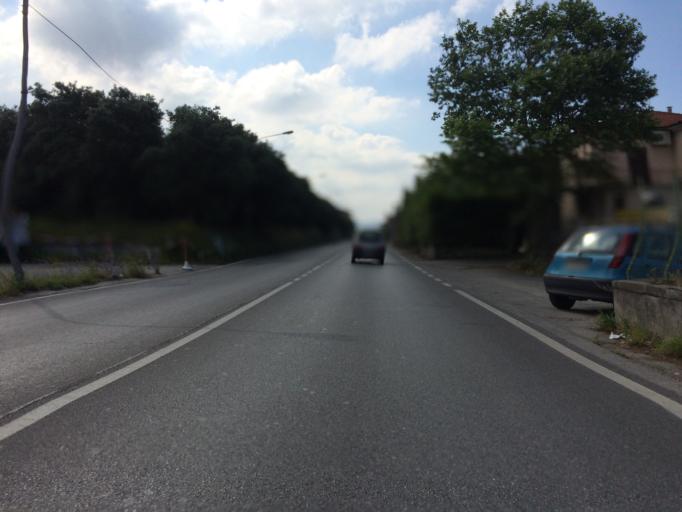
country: IT
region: Tuscany
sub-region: Provincia di Lucca
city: Ripa-Pozzi-Querceta-Ponterosso
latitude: 43.9736
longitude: 10.2044
